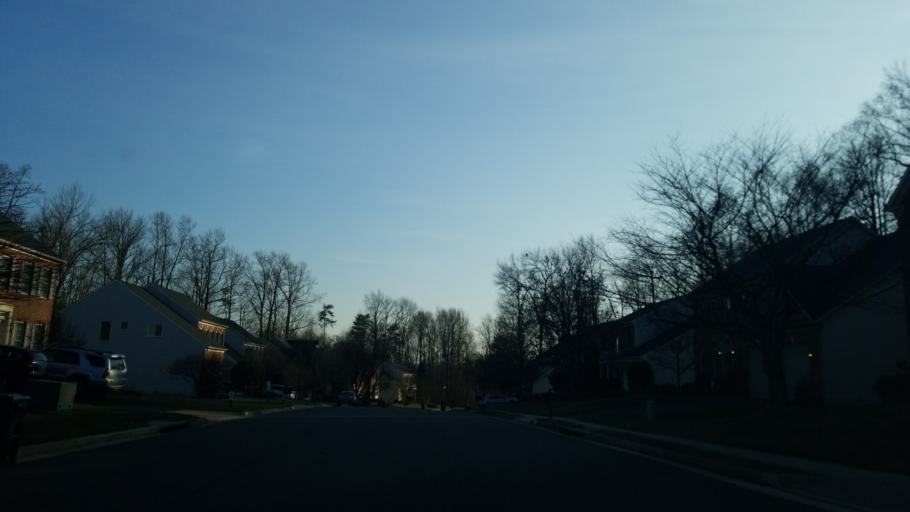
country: US
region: Virginia
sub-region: Fairfax County
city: Greenbriar
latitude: 38.8494
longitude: -77.3982
